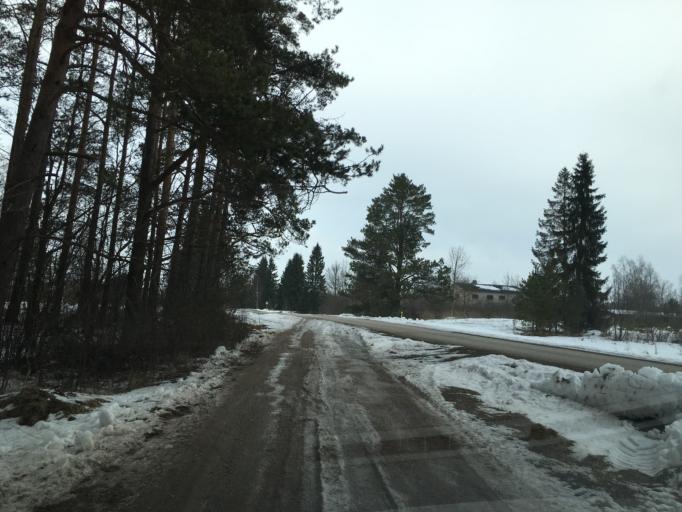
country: EE
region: Tartu
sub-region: Elva linn
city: Elva
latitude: 58.0891
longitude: 26.1984
